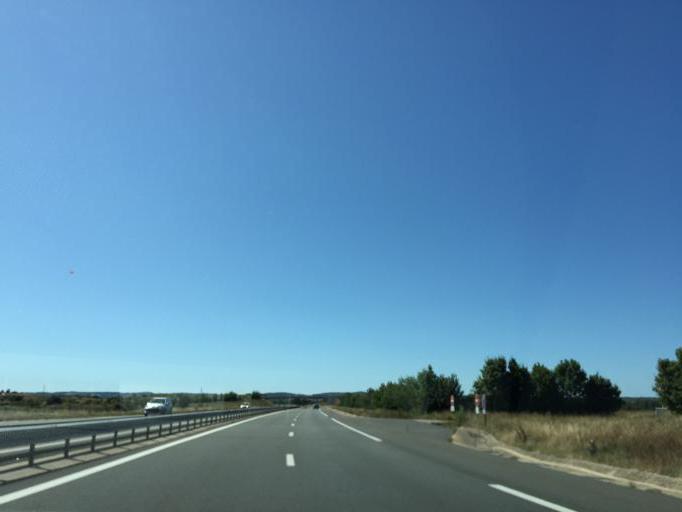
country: FR
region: Midi-Pyrenees
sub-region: Departement de l'Aveyron
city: La Cavalerie
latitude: 43.9653
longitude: 3.2099
